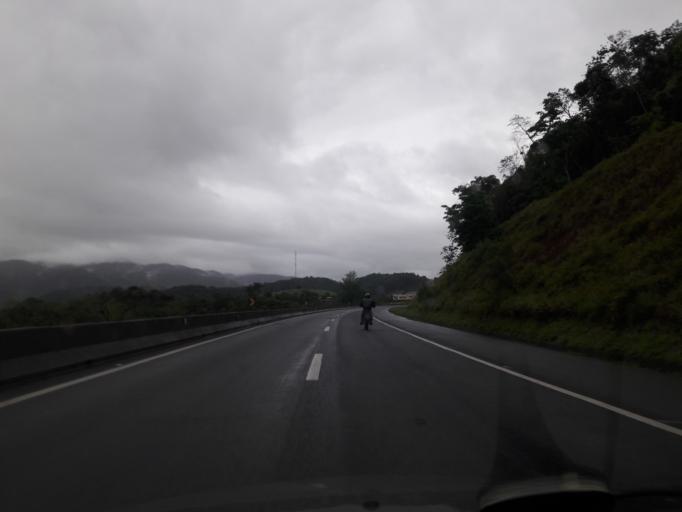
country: BR
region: Sao Paulo
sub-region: Miracatu
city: Miracatu
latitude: -24.2065
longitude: -47.3721
